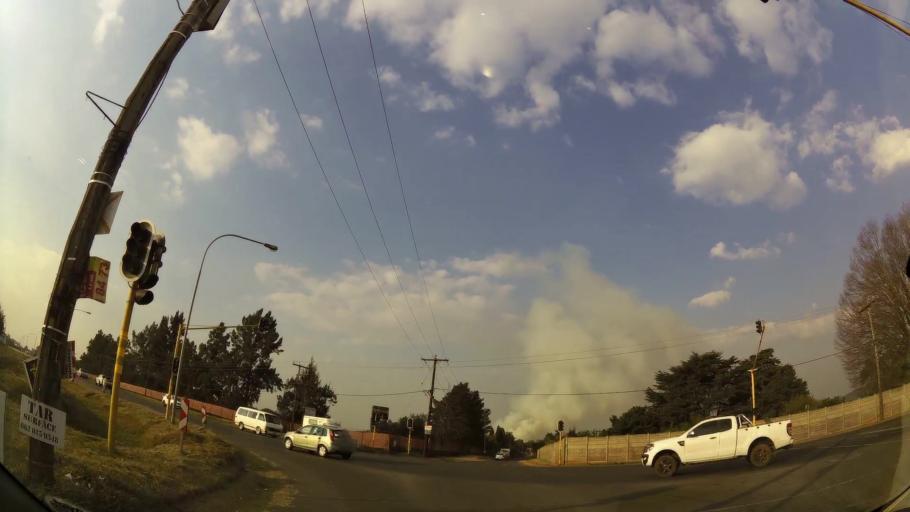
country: ZA
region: Gauteng
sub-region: Ekurhuleni Metropolitan Municipality
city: Benoni
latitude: -26.1211
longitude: 28.2937
